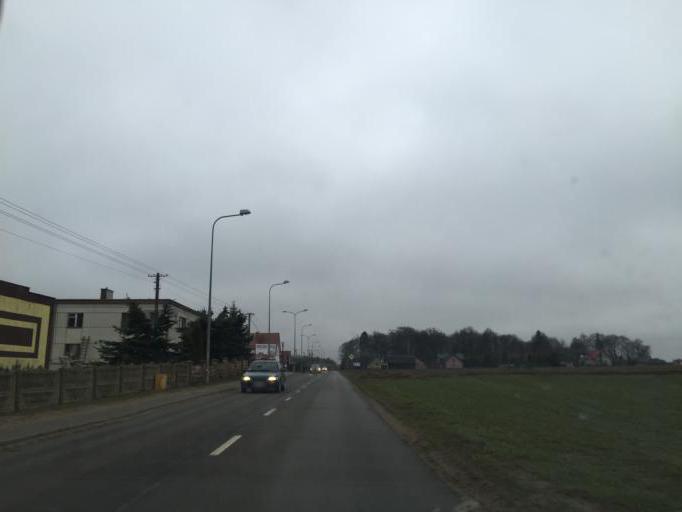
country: PL
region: Pomeranian Voivodeship
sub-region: Powiat kartuski
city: Banino
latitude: 54.3720
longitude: 18.4020
